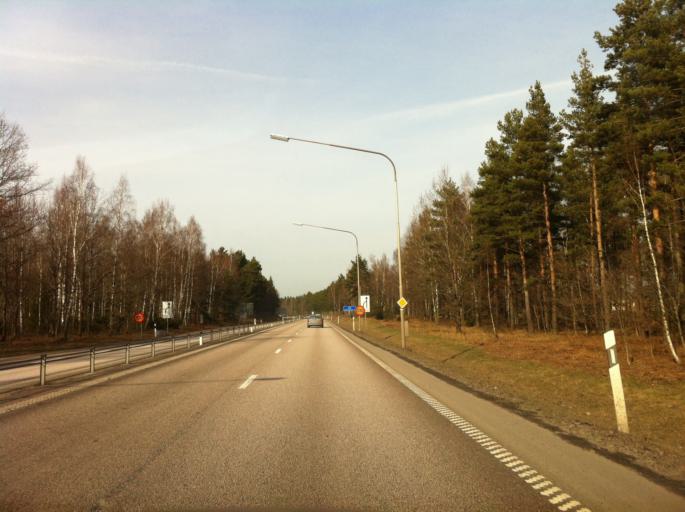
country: SE
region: Vaestra Goetaland
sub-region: Skovde Kommun
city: Skoevde
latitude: 58.4204
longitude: 13.8679
